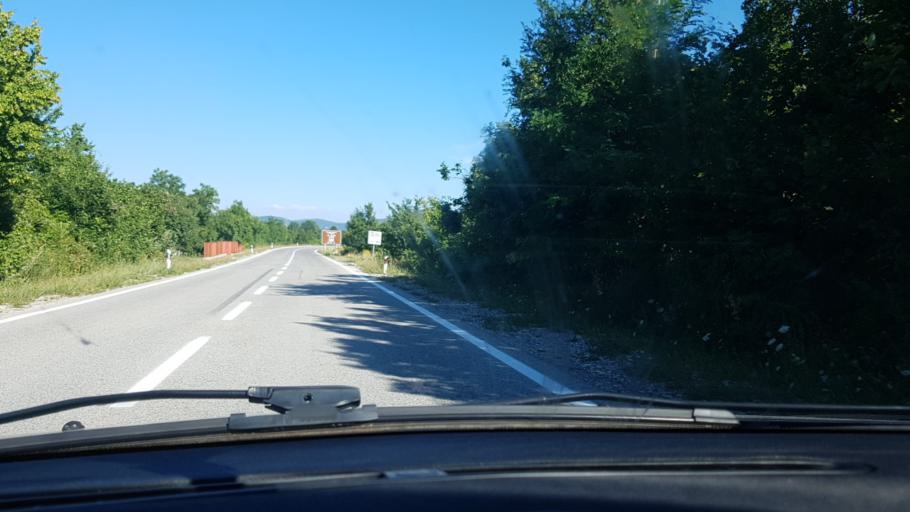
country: HR
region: Zadarska
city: Gracac
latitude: 44.2978
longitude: 15.8331
